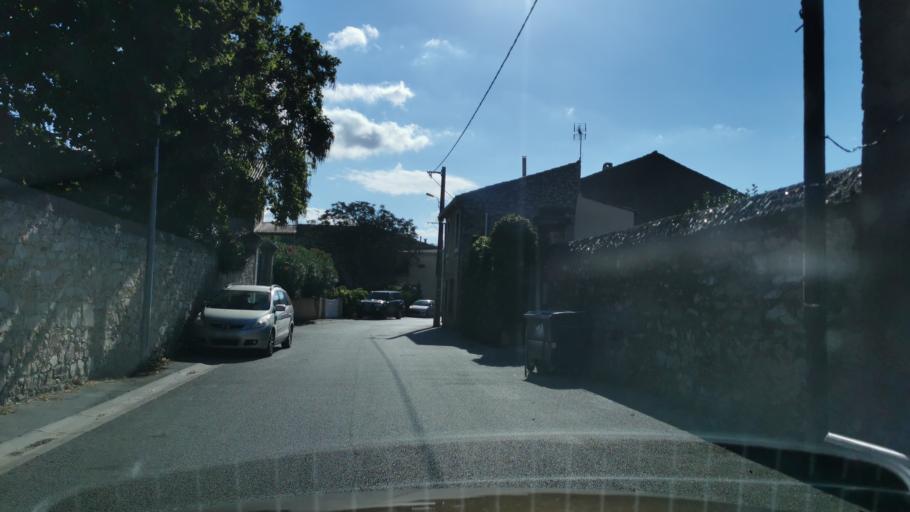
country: FR
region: Languedoc-Roussillon
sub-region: Departement de l'Aude
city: Canet
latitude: 43.2294
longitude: 2.8455
